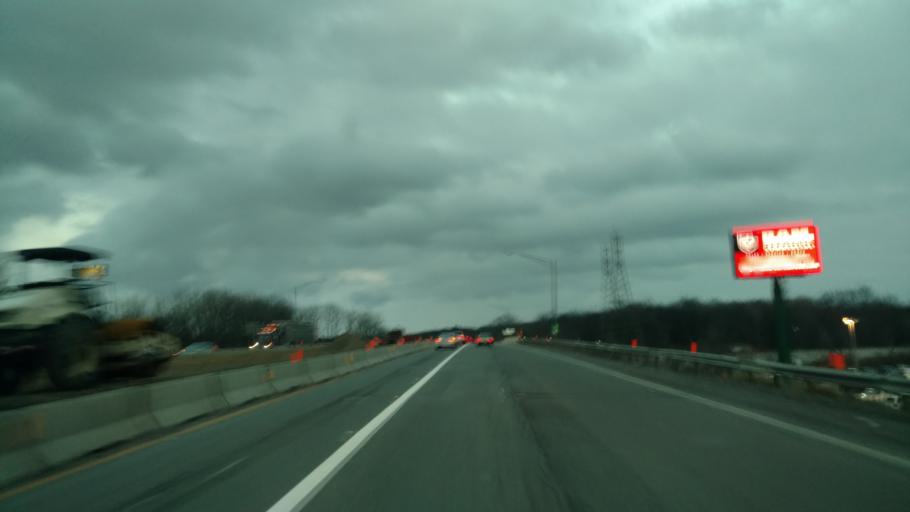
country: US
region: Ohio
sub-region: Summit County
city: Barberton
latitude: 41.0401
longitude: -81.6083
